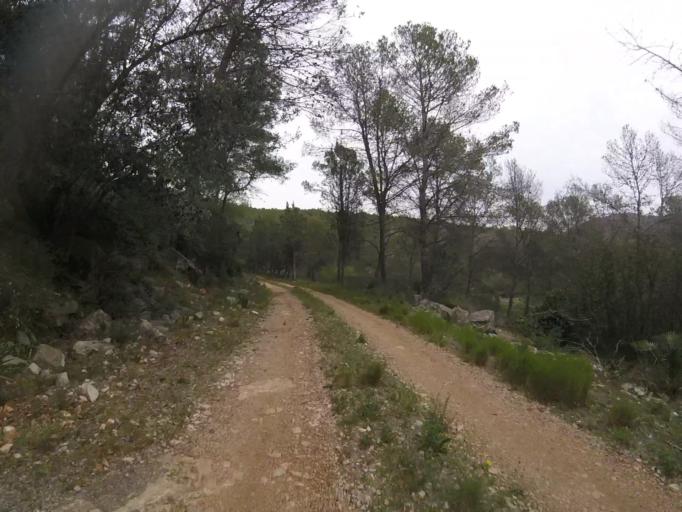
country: ES
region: Valencia
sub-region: Provincia de Castello
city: Santa Magdalena de Pulpis
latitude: 40.3202
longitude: 0.2821
